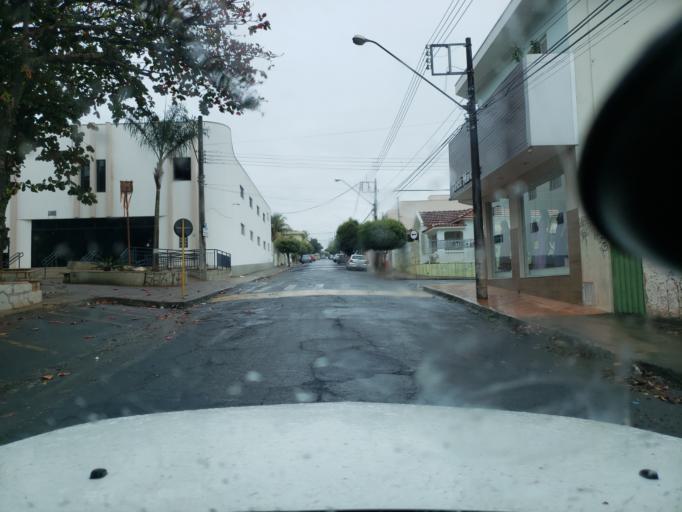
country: BR
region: Sao Paulo
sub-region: Moji-Guacu
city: Mogi-Gaucu
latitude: -22.3768
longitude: -46.9366
